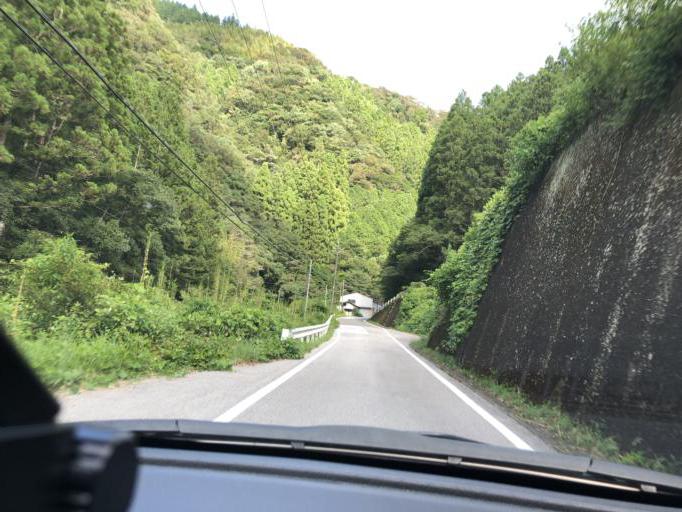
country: JP
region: Kochi
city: Kochi-shi
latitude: 33.6134
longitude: 133.4990
